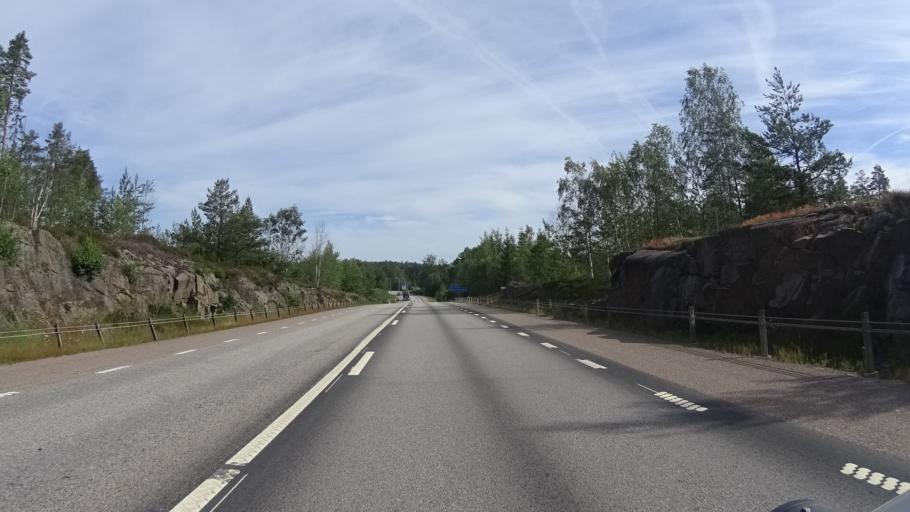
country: SE
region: Kalmar
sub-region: Vasterviks Kommun
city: Ankarsrum
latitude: 57.5848
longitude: 16.4859
